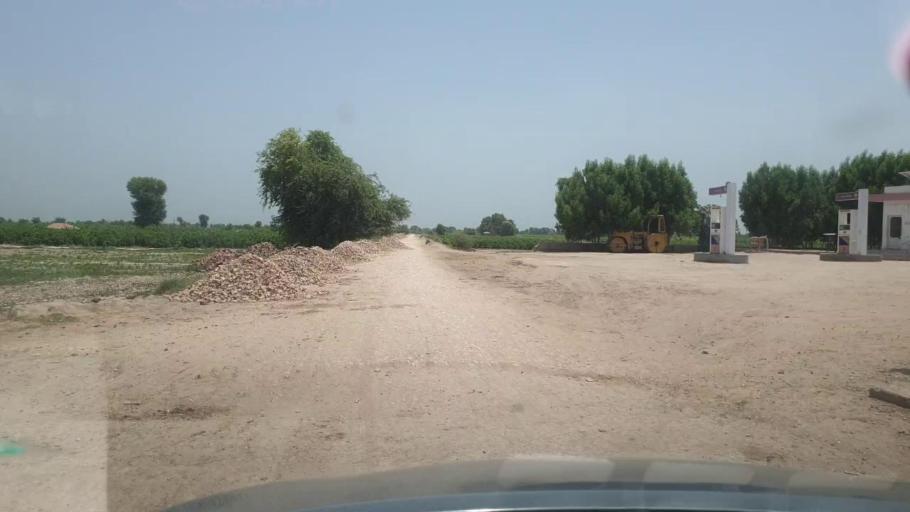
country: PK
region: Sindh
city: Hingorja
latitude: 27.2255
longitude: 68.3235
